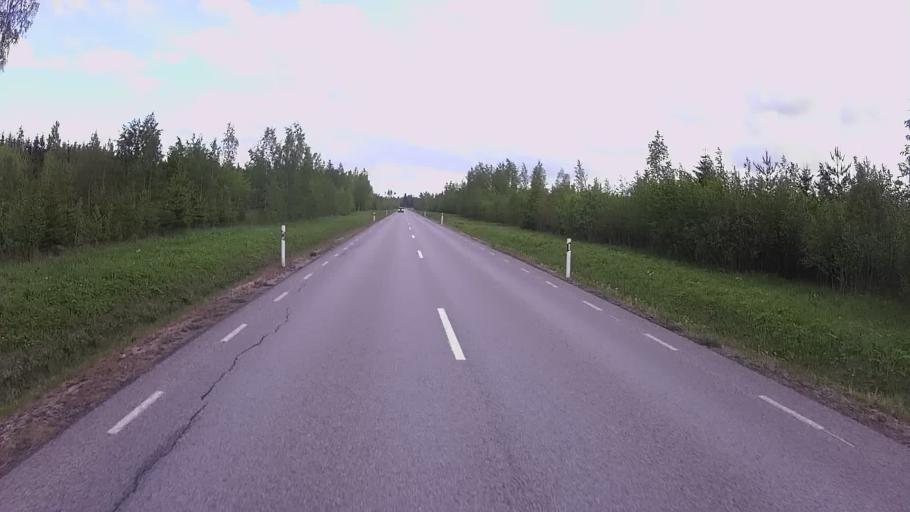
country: EE
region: Jogevamaa
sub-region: Mustvee linn
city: Mustvee
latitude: 59.0858
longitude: 26.9882
